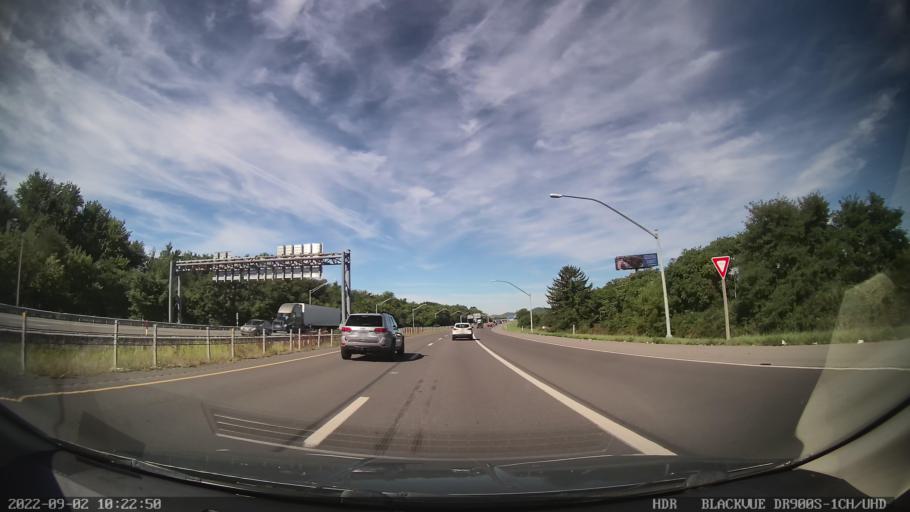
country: US
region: Pennsylvania
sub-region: Lycoming County
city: Duboistown
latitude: 41.2308
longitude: -77.0234
